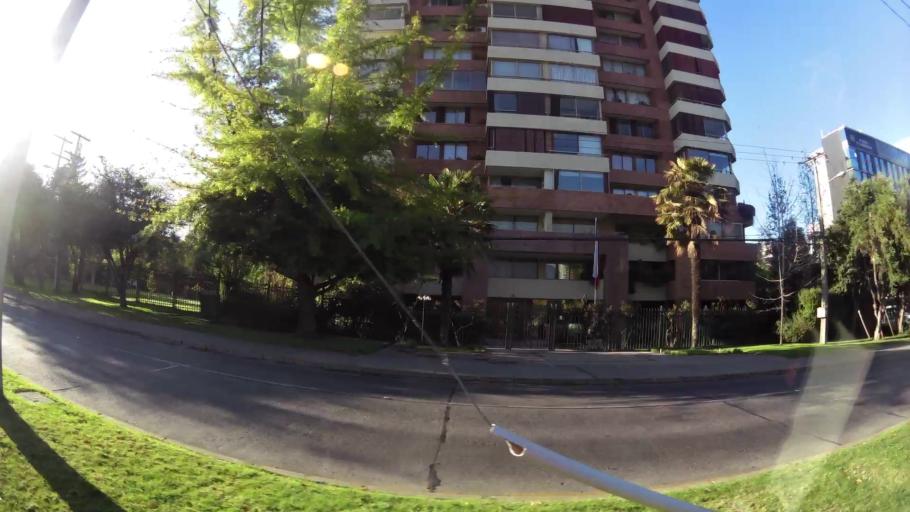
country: CL
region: Santiago Metropolitan
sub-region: Provincia de Santiago
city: Villa Presidente Frei, Nunoa, Santiago, Chile
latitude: -33.4021
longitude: -70.5691
